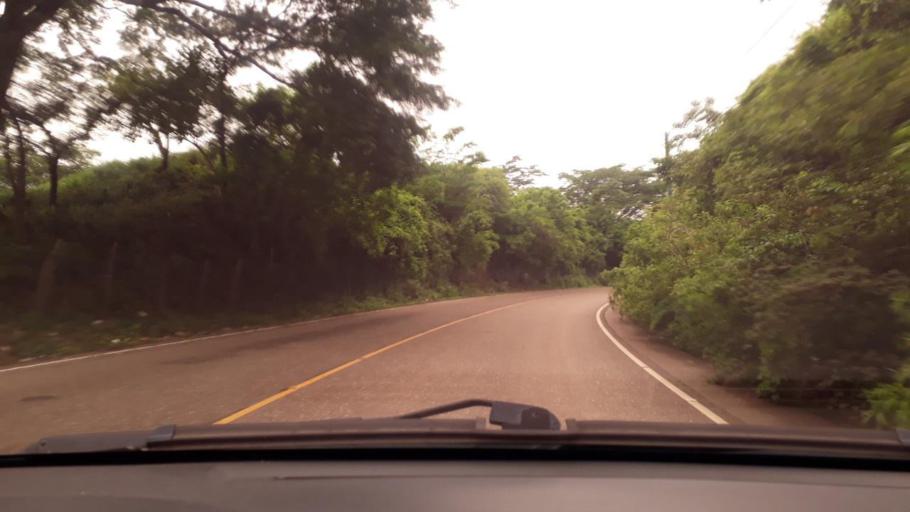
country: GT
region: Chiquimula
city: Concepcion Las Minas
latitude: 14.4357
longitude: -89.4584
